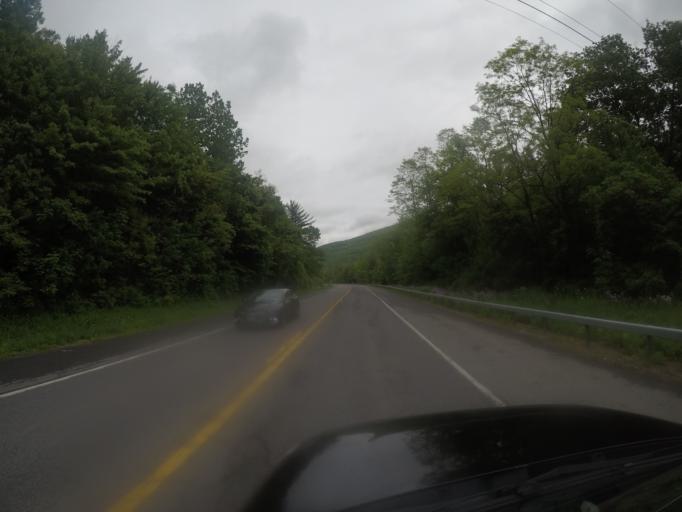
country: US
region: New York
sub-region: Ulster County
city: Shokan
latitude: 42.0732
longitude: -74.3070
